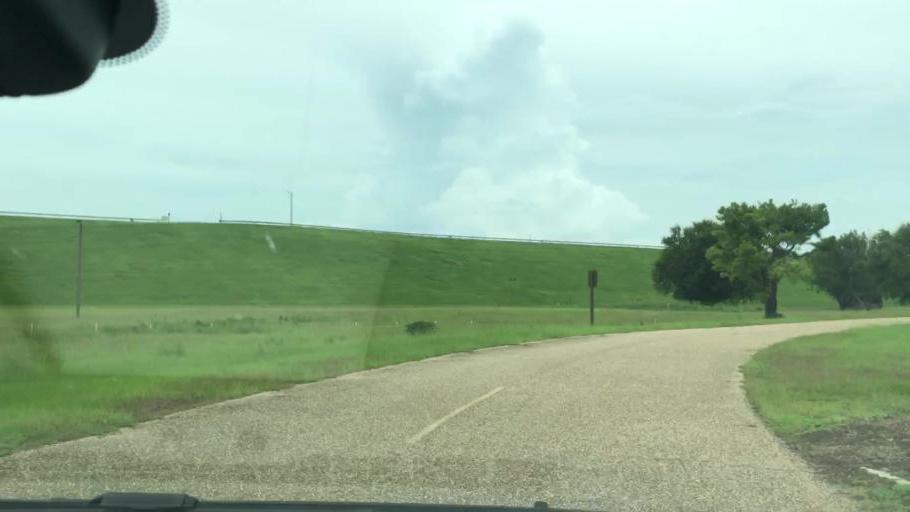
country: US
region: Georgia
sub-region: Clay County
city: Fort Gaines
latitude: 31.6268
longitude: -85.0606
